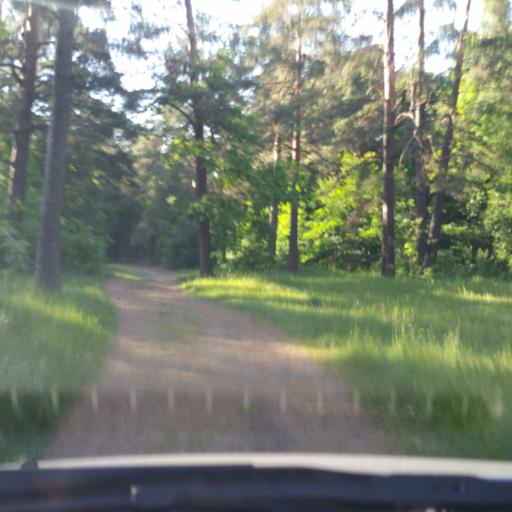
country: LV
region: Riga
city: Jaunciems
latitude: 56.9790
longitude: 24.2043
